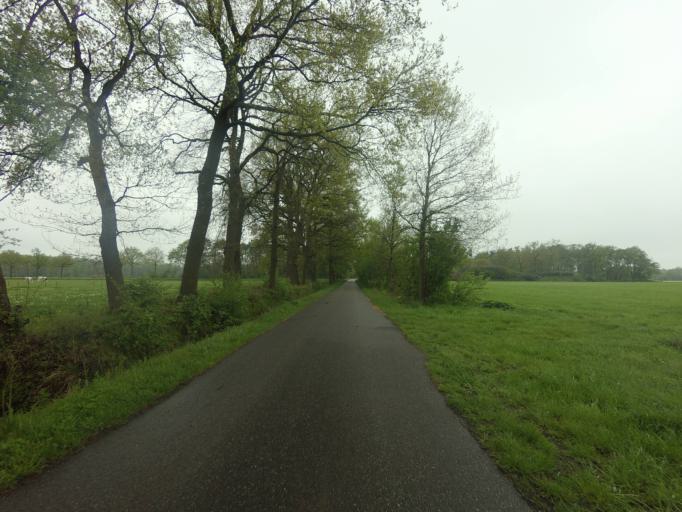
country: DE
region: North Rhine-Westphalia
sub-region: Regierungsbezirk Munster
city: Vreden
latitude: 52.1298
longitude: 6.8503
